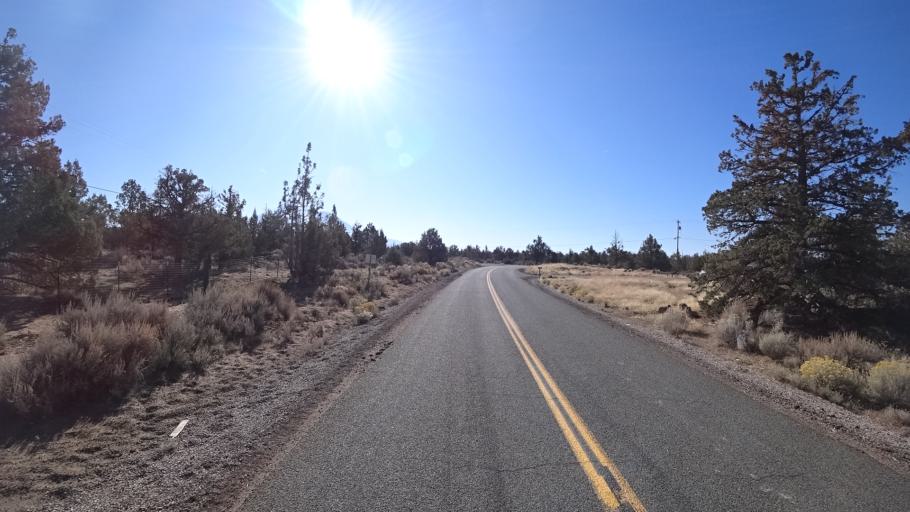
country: US
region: California
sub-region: Siskiyou County
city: Weed
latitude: 41.5899
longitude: -122.3017
